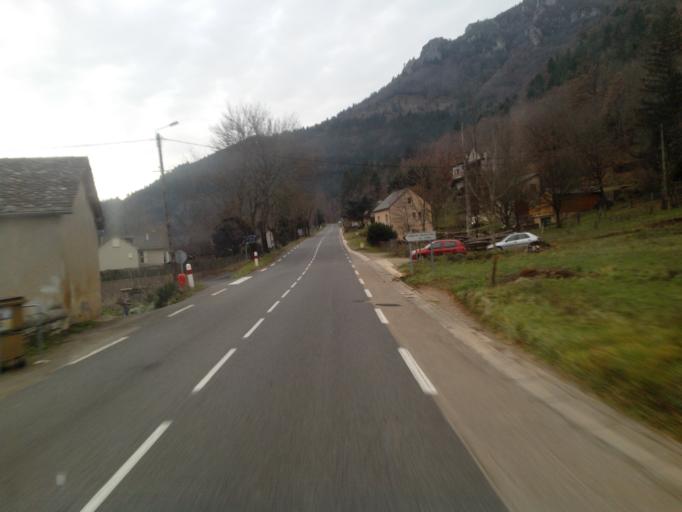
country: FR
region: Languedoc-Roussillon
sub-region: Departement de la Lozere
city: Florac
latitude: 44.3101
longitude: 3.5984
